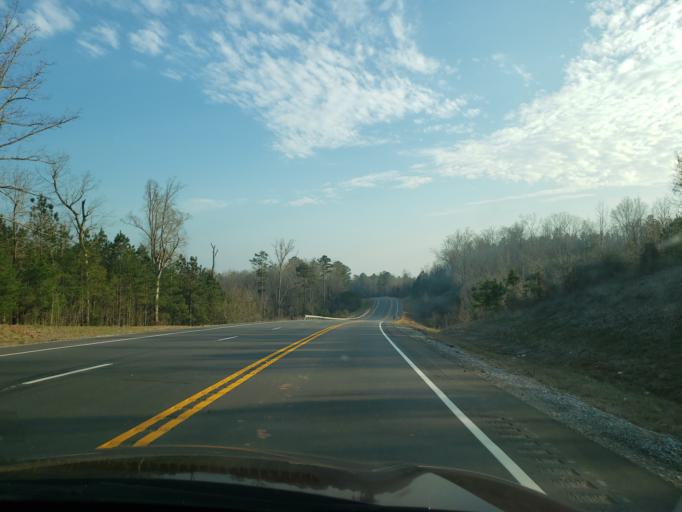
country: US
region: Alabama
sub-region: Hale County
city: Moundville
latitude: 32.8617
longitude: -87.6131
